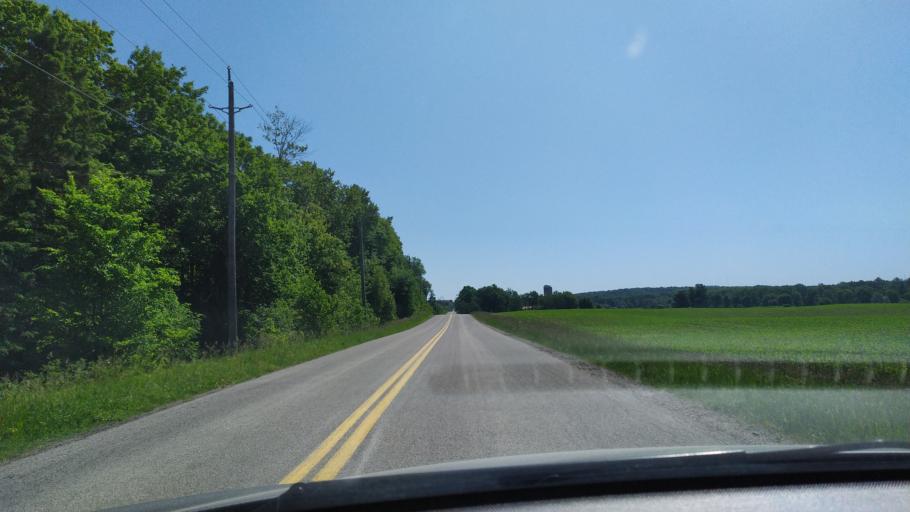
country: CA
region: Ontario
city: Waterloo
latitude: 43.4627
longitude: -80.6922
